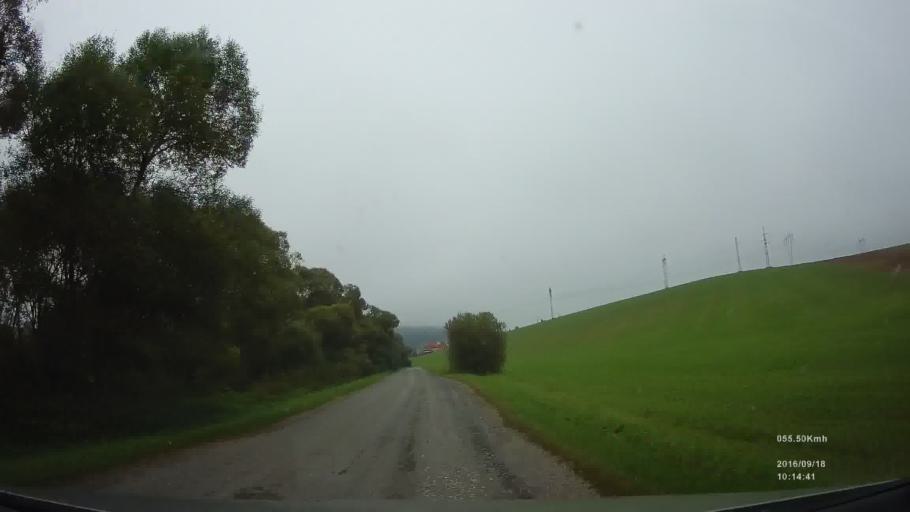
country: SK
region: Kosicky
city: Spisska Nova Ves
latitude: 48.9419
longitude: 20.6245
